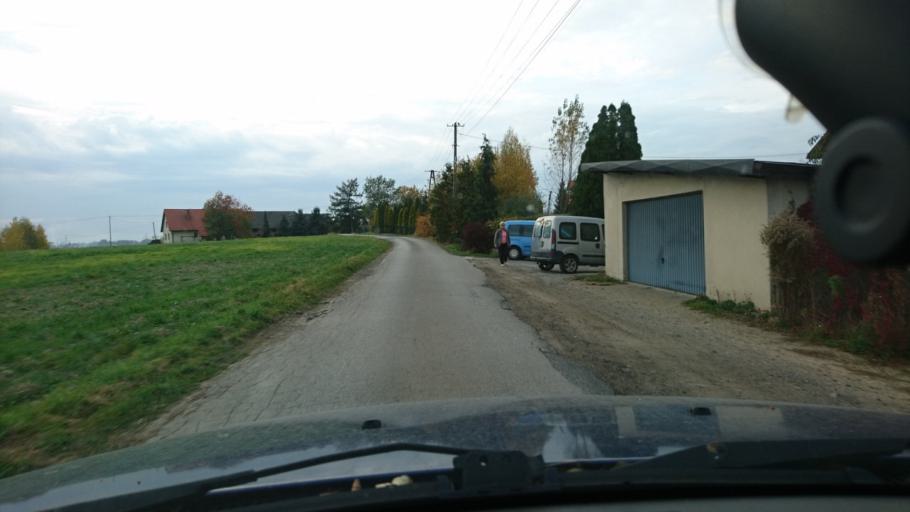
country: PL
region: Silesian Voivodeship
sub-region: Powiat bielski
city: Kozy
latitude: 49.8653
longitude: 19.1569
